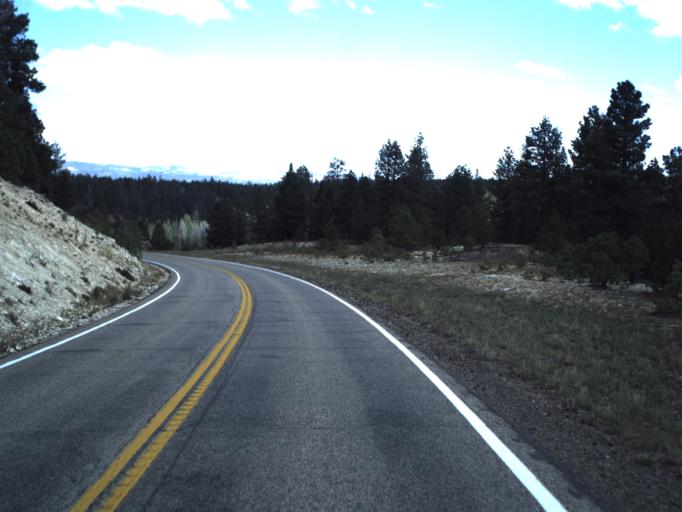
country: US
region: Utah
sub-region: Garfield County
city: Panguitch
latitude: 37.4911
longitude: -112.6149
